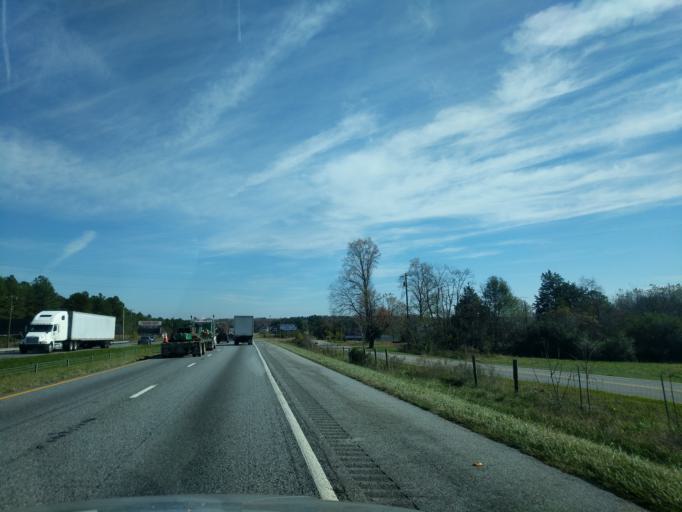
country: US
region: South Carolina
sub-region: Spartanburg County
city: Cowpens
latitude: 35.0752
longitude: -81.7392
